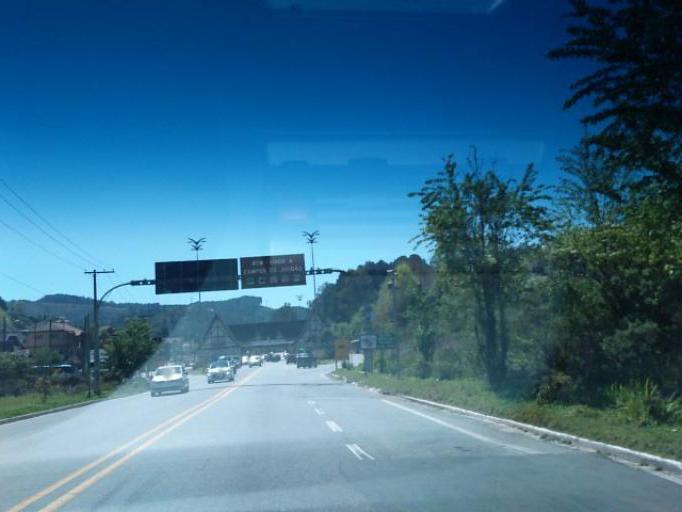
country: BR
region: Sao Paulo
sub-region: Campos Do Jordao
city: Campos do Jordao
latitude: -22.7565
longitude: -45.6104
